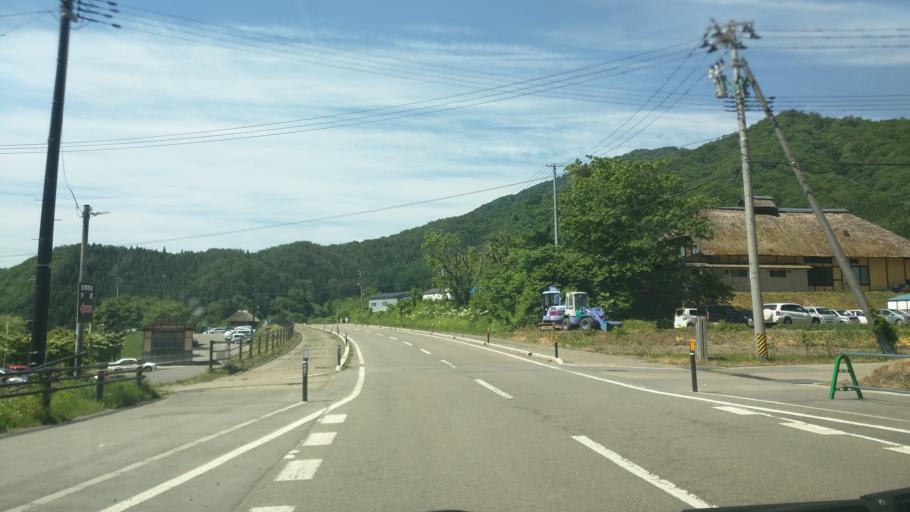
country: JP
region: Fukushima
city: Kitakata
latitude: 37.3323
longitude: 139.8616
